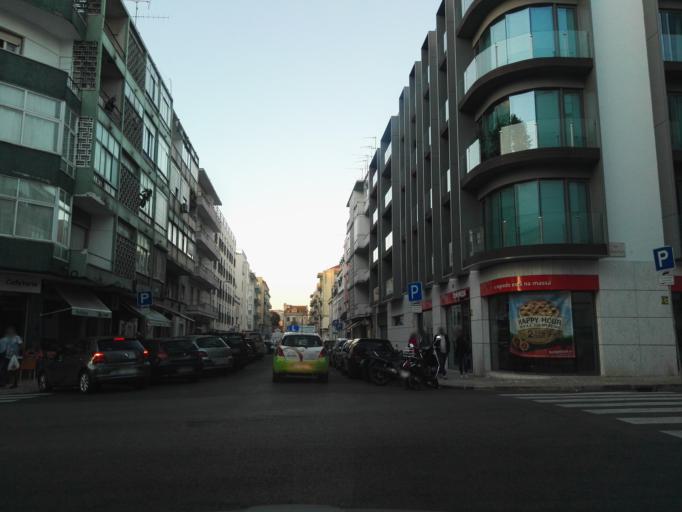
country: PT
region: Lisbon
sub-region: Lisbon
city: Lisbon
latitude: 38.7193
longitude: -9.1651
